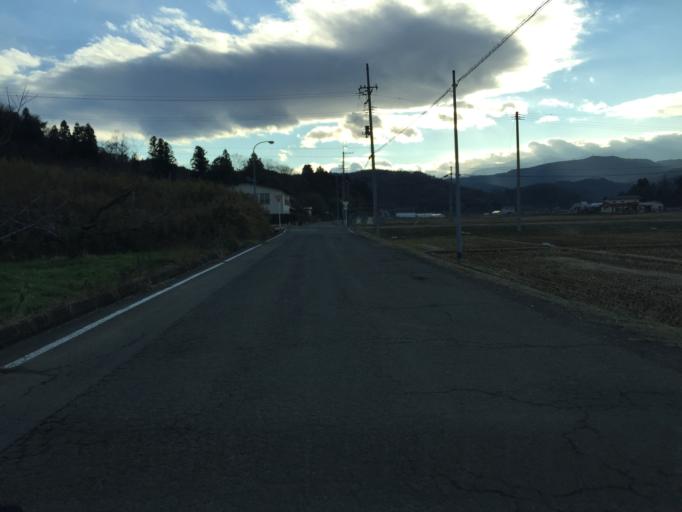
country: JP
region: Fukushima
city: Fukushima-shi
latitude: 37.7095
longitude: 140.4410
